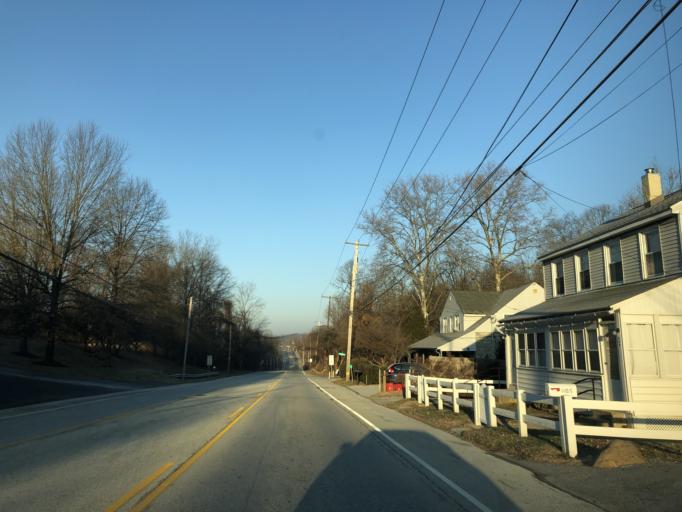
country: US
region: Pennsylvania
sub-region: Chester County
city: West Chester
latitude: 39.9614
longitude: -75.6215
